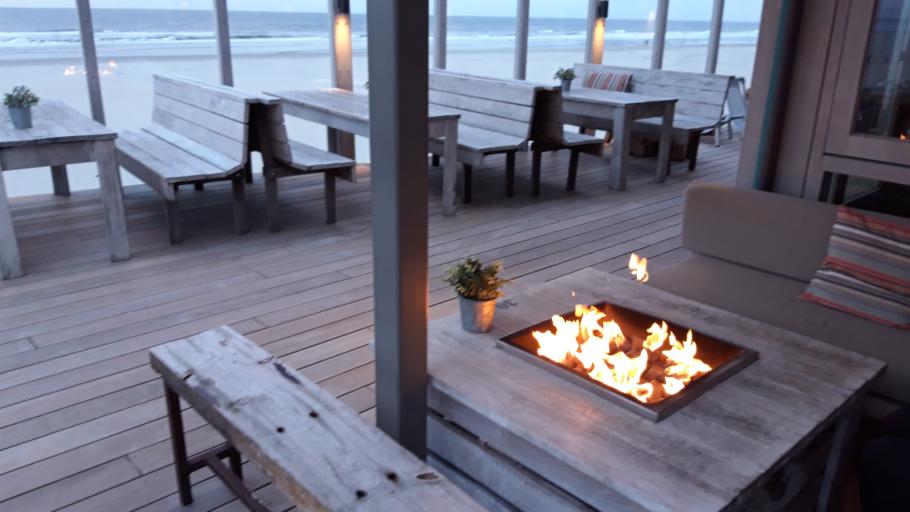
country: NL
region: Friesland
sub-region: Gemeente Ameland
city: Nes
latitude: 53.4603
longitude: 5.7786
